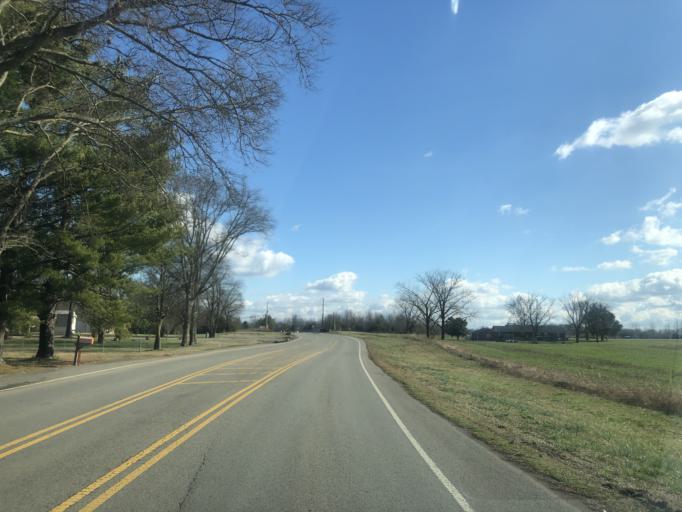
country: US
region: Tennessee
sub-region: Rutherford County
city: Smyrna
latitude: 35.8756
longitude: -86.5011
